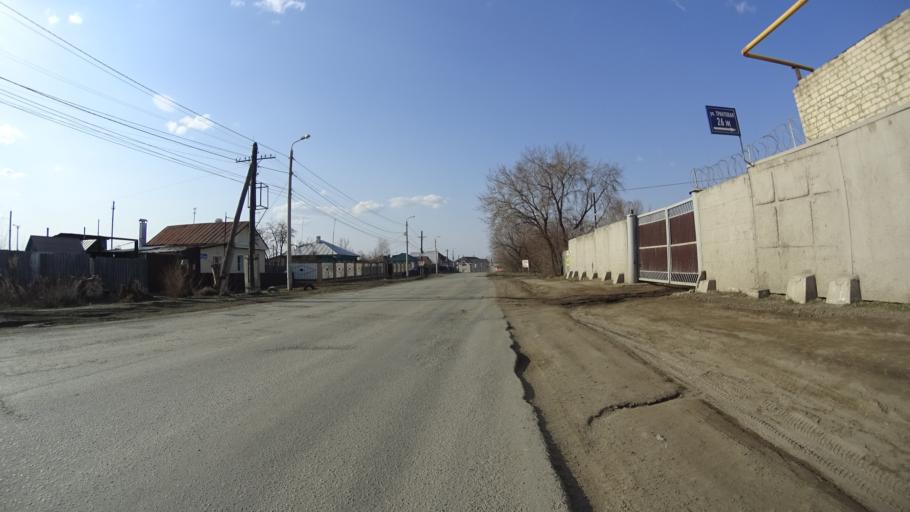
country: RU
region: Chelyabinsk
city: Novosineglazovskiy
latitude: 55.1092
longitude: 61.3337
